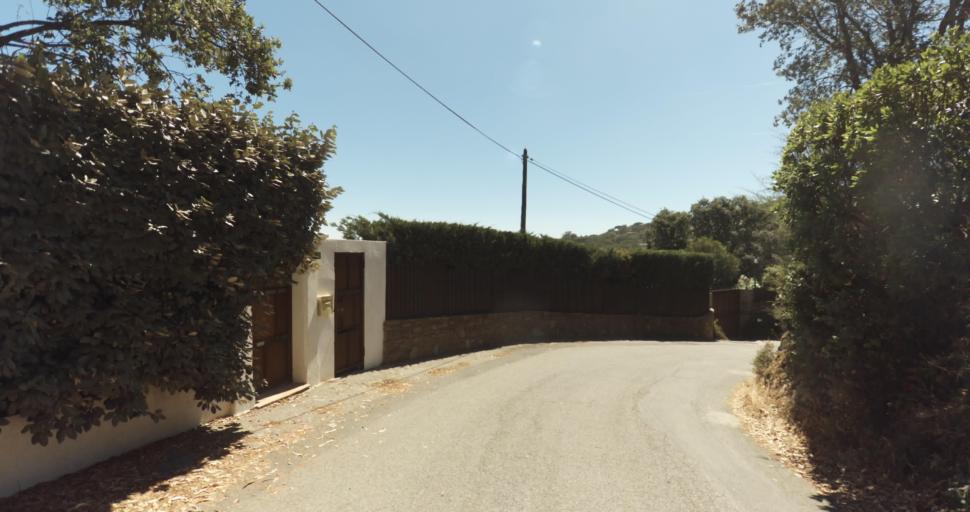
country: FR
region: Provence-Alpes-Cote d'Azur
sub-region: Departement du Var
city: Saint-Tropez
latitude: 43.2629
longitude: 6.6068
